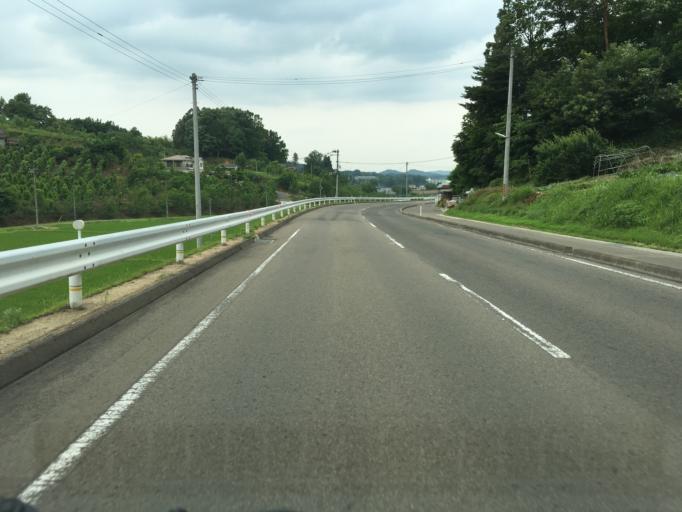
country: JP
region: Fukushima
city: Nihommatsu
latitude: 37.6453
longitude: 140.5354
